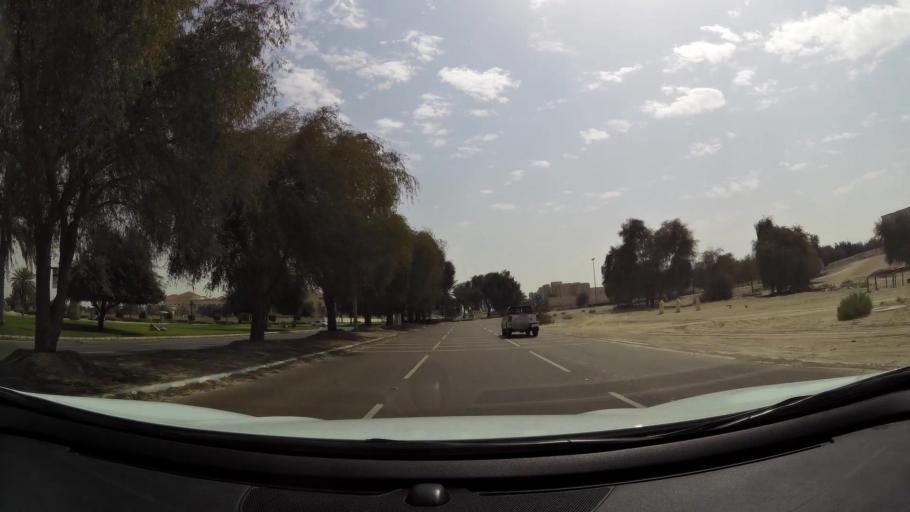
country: AE
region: Abu Dhabi
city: Abu Dhabi
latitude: 24.3080
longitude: 54.6173
